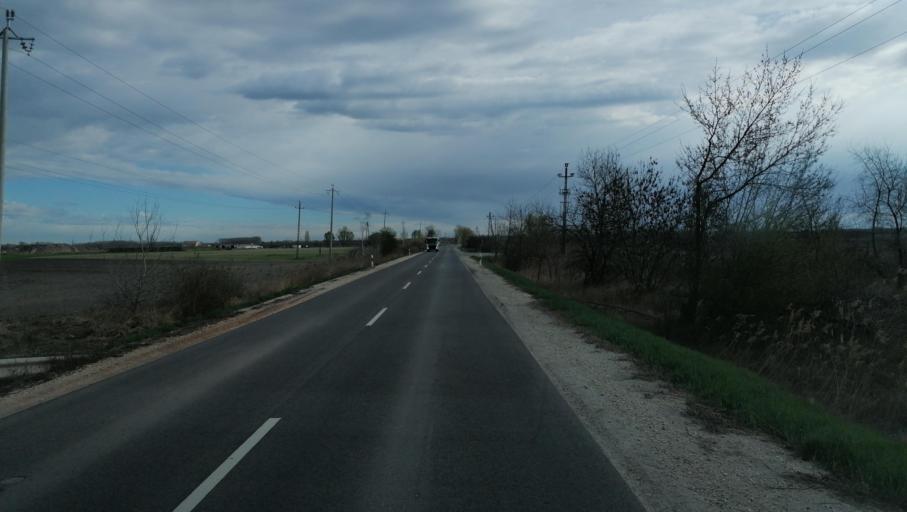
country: HU
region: Pest
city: Bugyi
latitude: 47.2446
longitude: 19.1976
